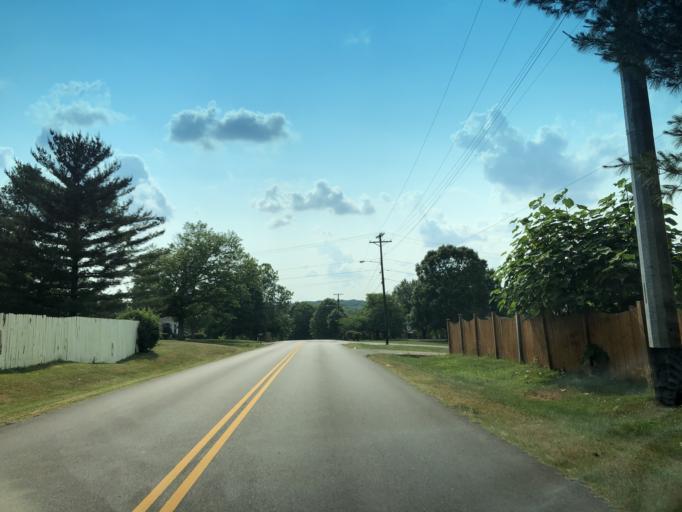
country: US
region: Tennessee
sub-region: Davidson County
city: Goodlettsville
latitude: 36.2737
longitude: -86.7206
